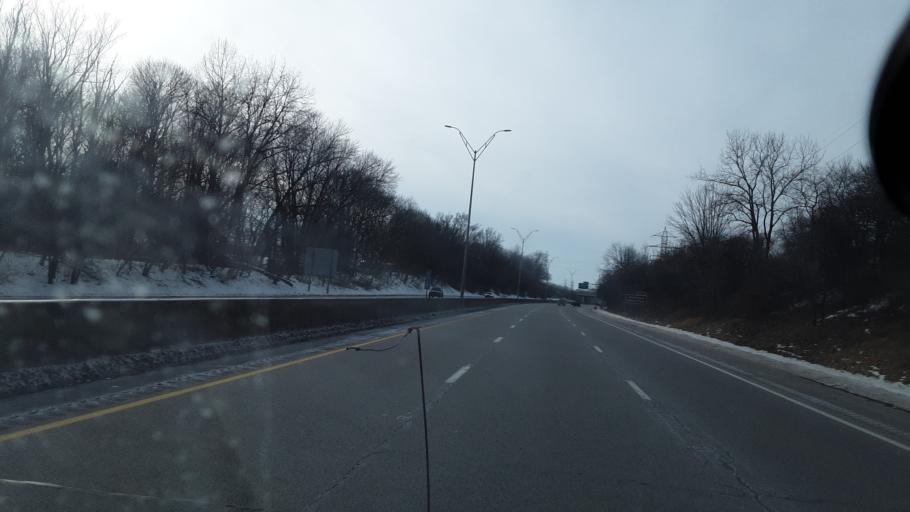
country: US
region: Ohio
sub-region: Summit County
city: Portage Lakes
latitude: 41.0248
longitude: -81.5187
